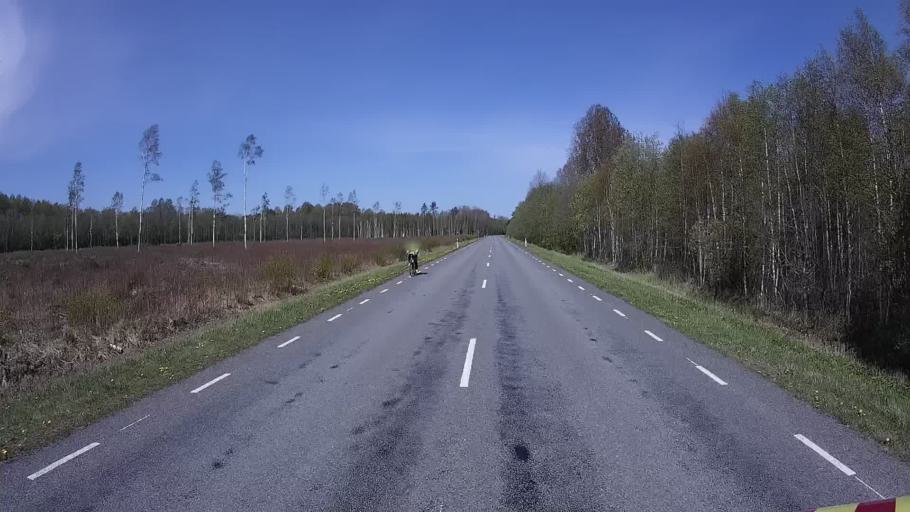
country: EE
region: Laeaene
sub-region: Lihula vald
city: Lihula
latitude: 58.6468
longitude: 23.8460
